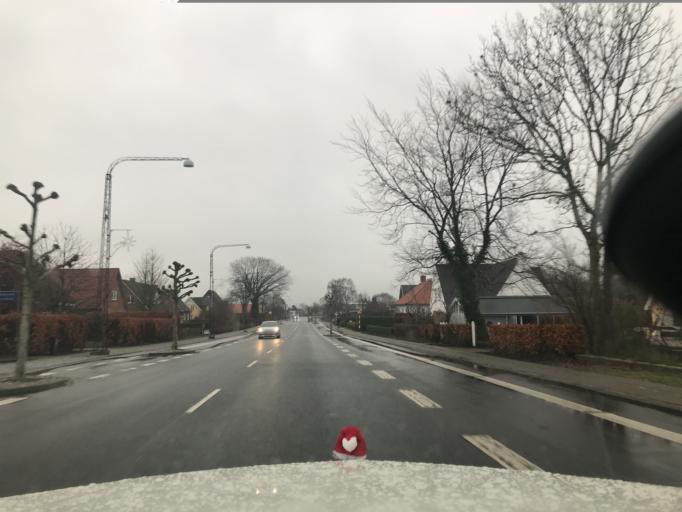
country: DK
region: South Denmark
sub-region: Aabenraa Kommune
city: Rodekro
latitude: 55.0705
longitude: 9.3413
